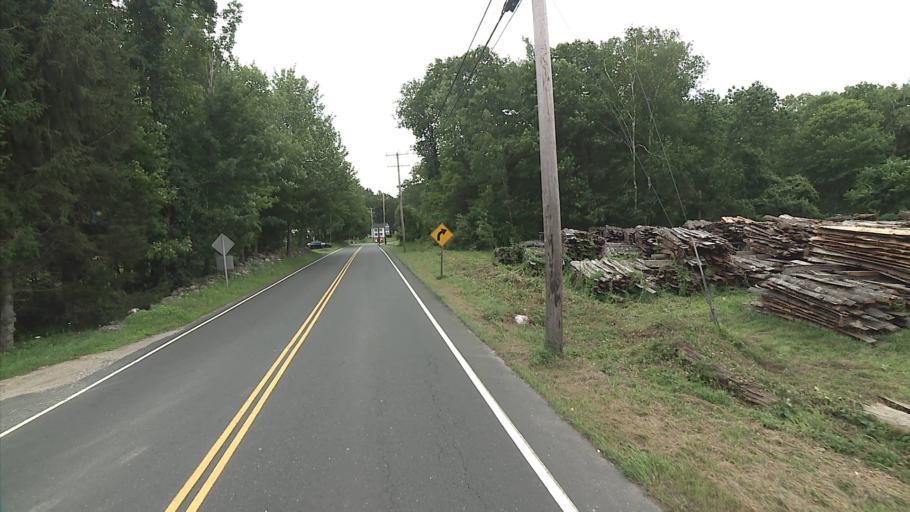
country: US
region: Connecticut
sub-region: Litchfield County
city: Winsted
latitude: 41.9868
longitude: -73.0463
